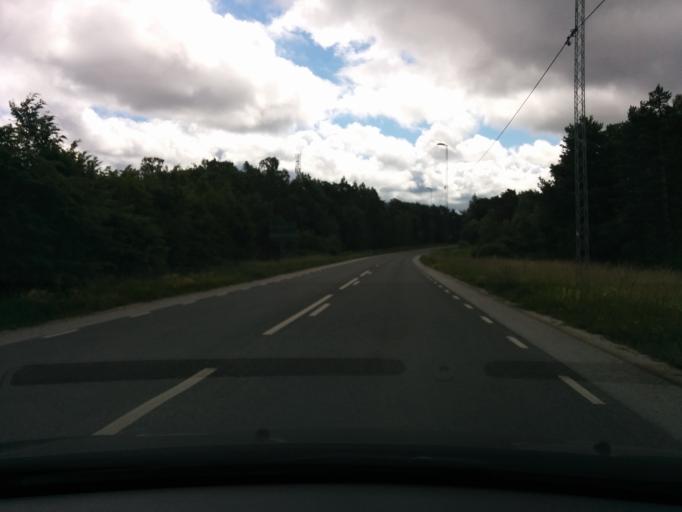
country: SE
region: Gotland
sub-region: Gotland
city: Visby
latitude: 57.6151
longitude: 18.2865
